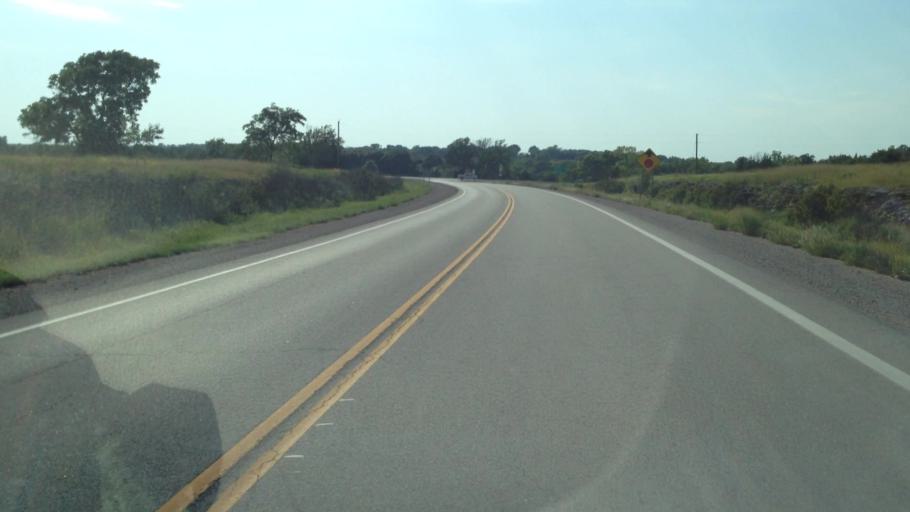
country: US
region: Kansas
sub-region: Anderson County
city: Garnett
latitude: 38.1965
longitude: -95.2476
